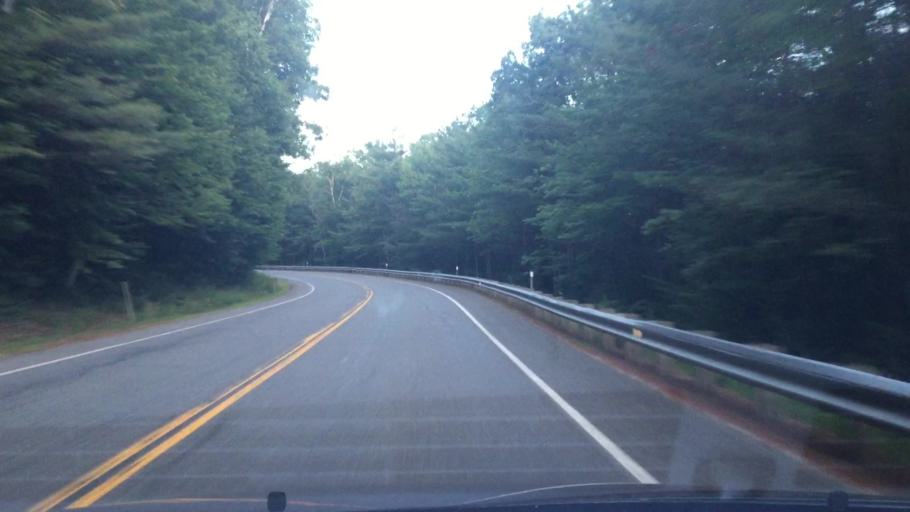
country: US
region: New Hampshire
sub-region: Grafton County
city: Woodstock
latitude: 44.0533
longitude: -71.5817
